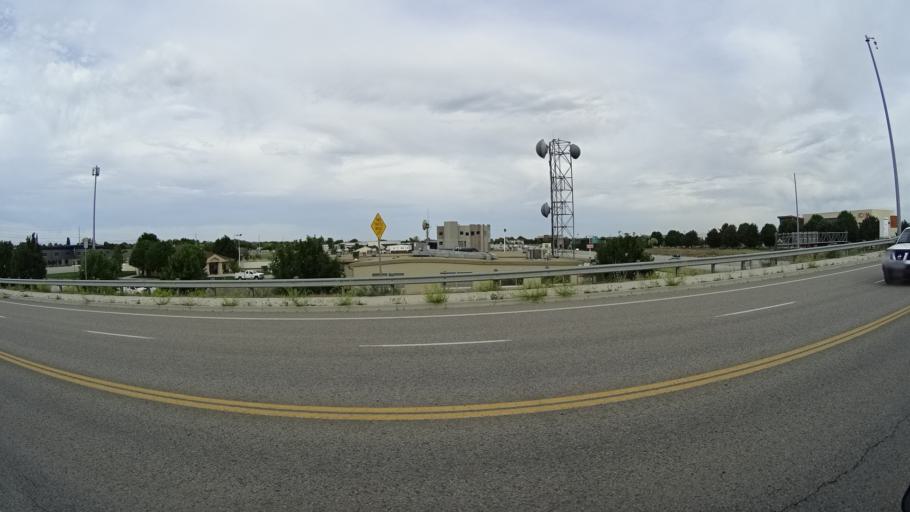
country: US
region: Idaho
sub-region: Ada County
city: Meridian
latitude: 43.5922
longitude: -116.3746
